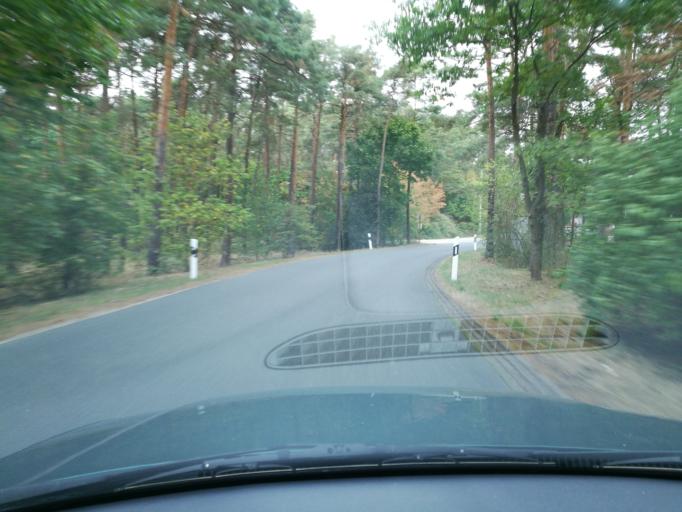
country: DE
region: Bavaria
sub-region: Regierungsbezirk Mittelfranken
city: Furth
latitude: 49.5063
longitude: 10.9850
